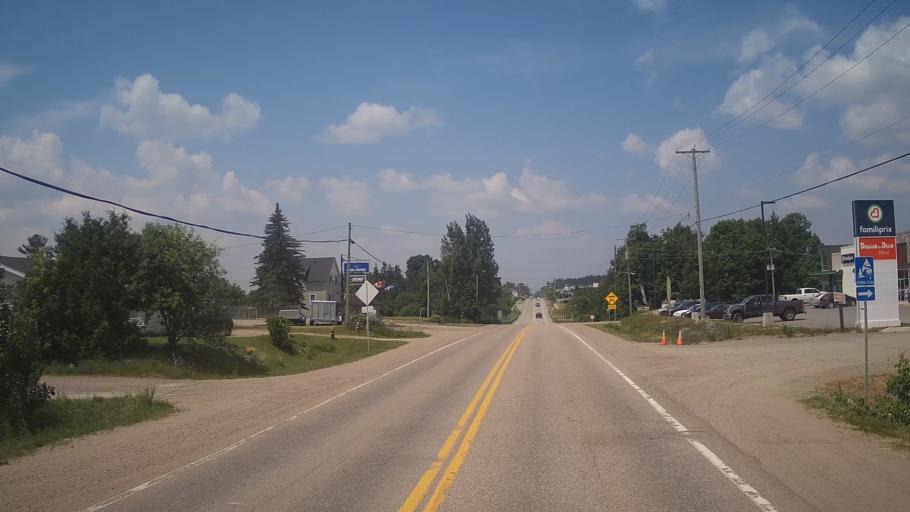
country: CA
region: Quebec
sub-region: Outaouais
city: Shawville
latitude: 45.5971
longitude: -76.4868
